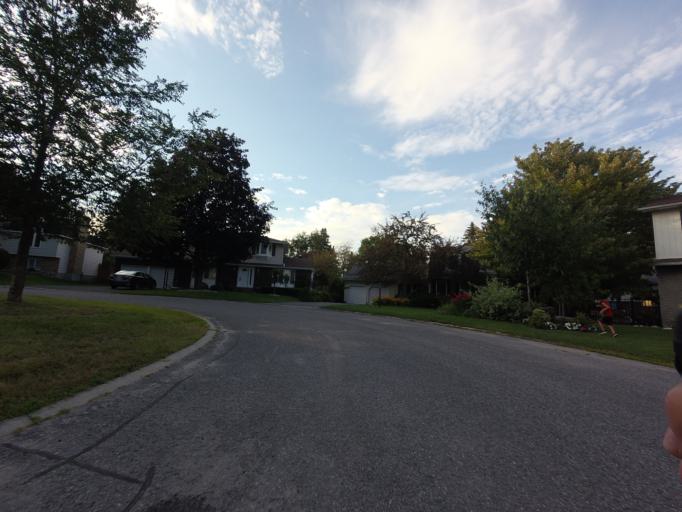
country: CA
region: Ontario
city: Bells Corners
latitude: 45.2813
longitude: -75.7663
